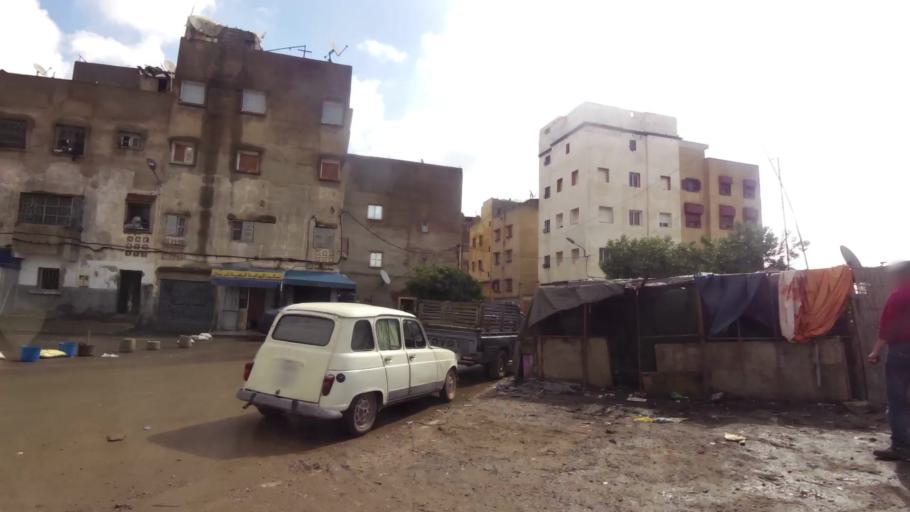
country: MA
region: Grand Casablanca
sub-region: Casablanca
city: Casablanca
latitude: 33.5304
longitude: -7.6696
